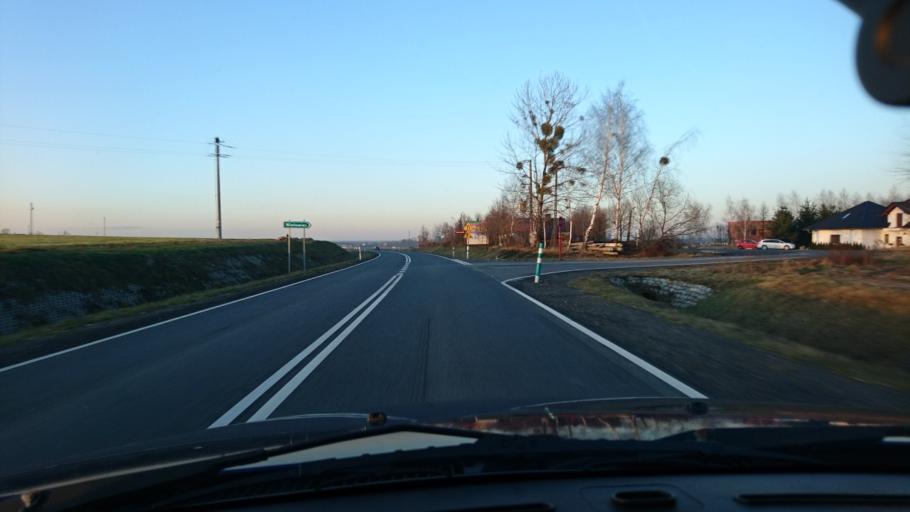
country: PL
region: Silesian Voivodeship
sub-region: Powiat gliwicki
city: Wielowies
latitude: 50.4936
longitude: 18.6075
